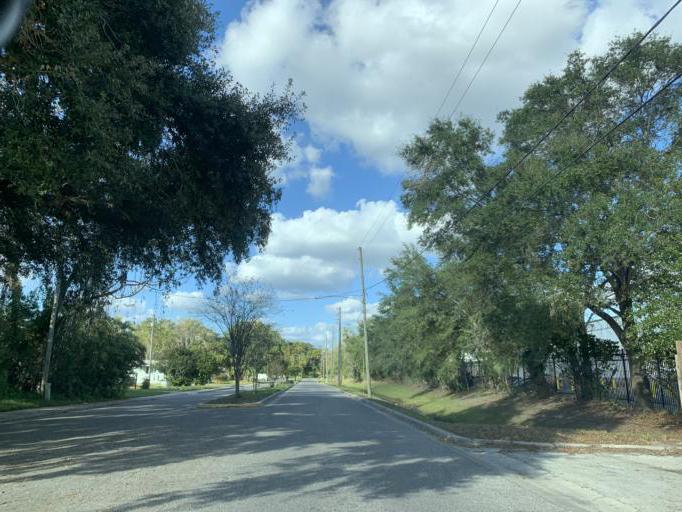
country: US
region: Florida
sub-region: Orange County
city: Eatonville
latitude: 28.6164
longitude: -81.3941
